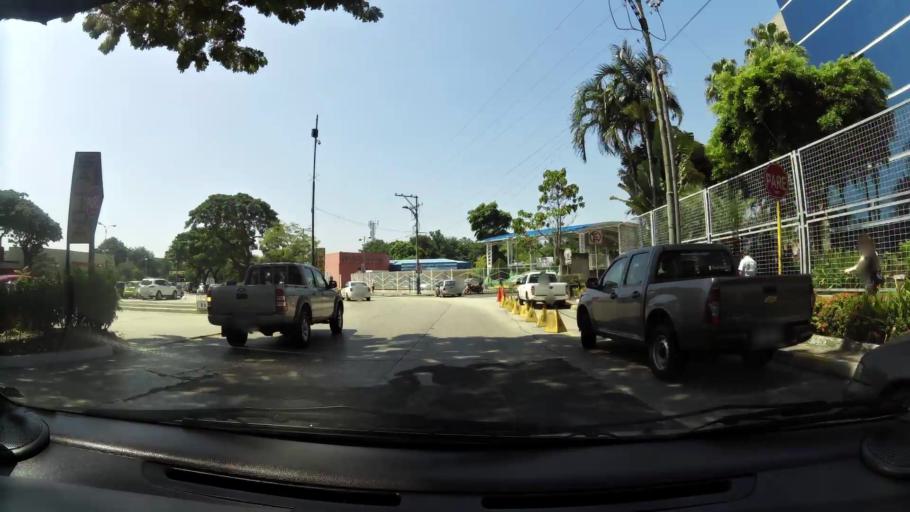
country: EC
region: Guayas
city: Guayaquil
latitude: -2.1701
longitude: -79.9166
